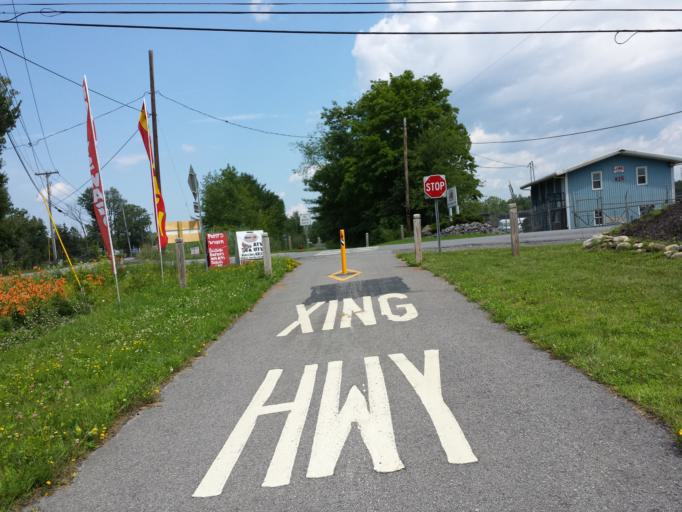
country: US
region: New York
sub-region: Saratoga County
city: Ballston Spa
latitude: 42.9718
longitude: -73.8366
